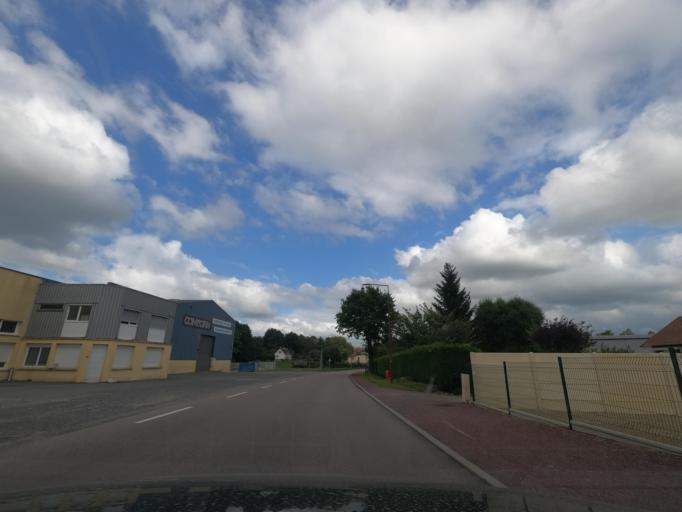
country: FR
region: Lower Normandy
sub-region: Departement de l'Orne
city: La Ferriere-aux-Etangs
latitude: 48.6658
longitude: -0.5146
